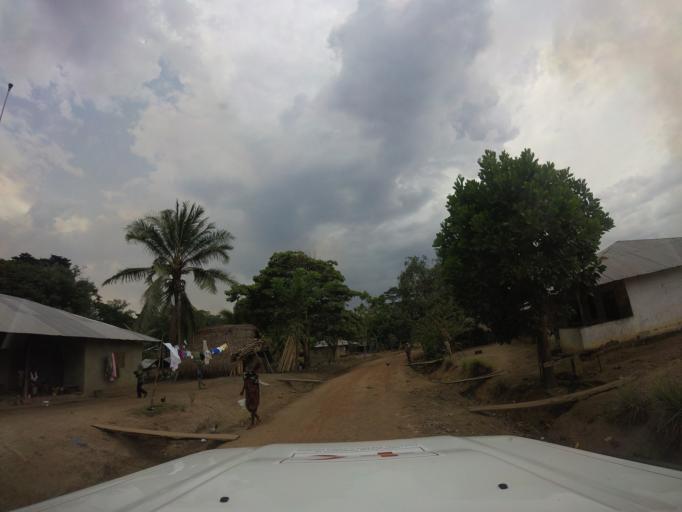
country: SL
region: Southern Province
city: Zimmi
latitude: 7.1360
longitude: -11.2834
